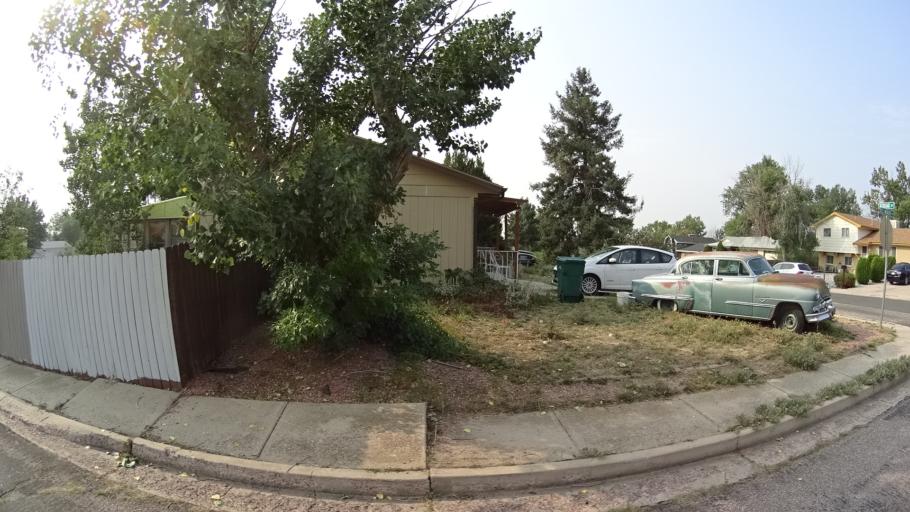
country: US
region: Colorado
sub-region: El Paso County
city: Stratmoor
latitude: 38.8033
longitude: -104.7682
